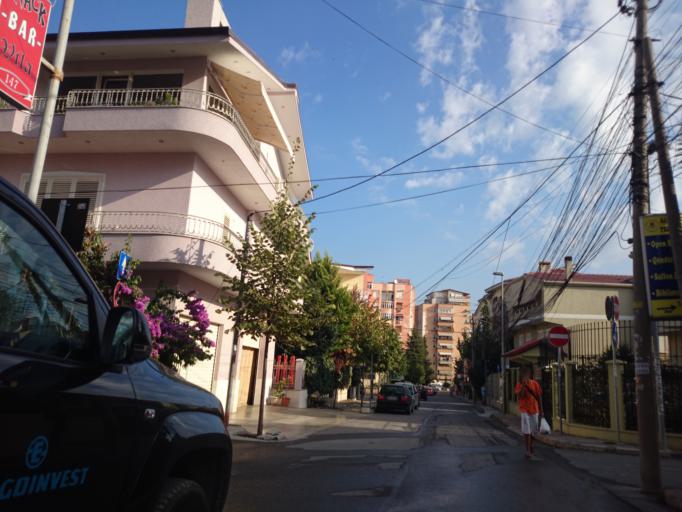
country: AL
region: Tirane
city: Tirana
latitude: 41.3168
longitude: 19.7996
